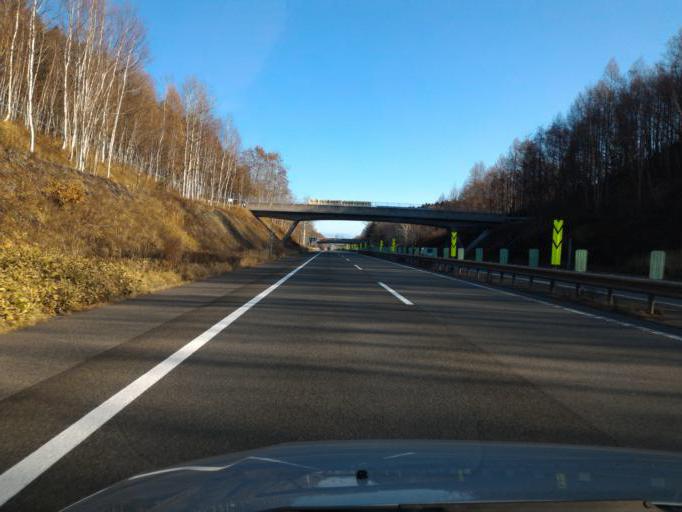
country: JP
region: Hokkaido
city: Iwamizawa
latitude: 43.1859
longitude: 141.7864
